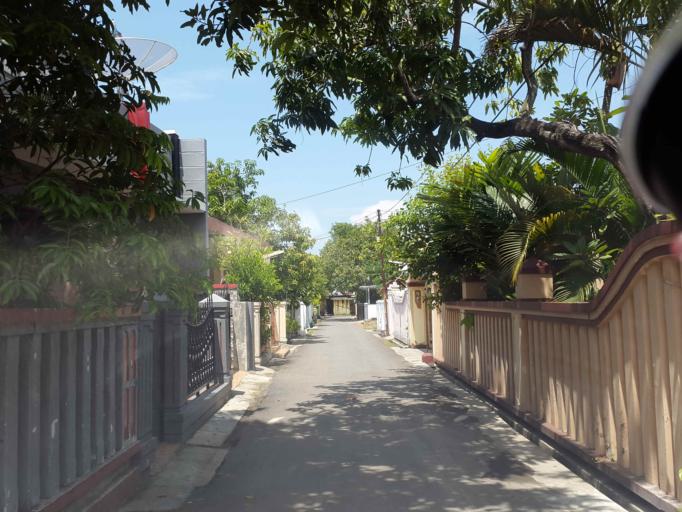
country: ID
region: Central Java
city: Dukuhturi
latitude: -6.8795
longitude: 109.0397
